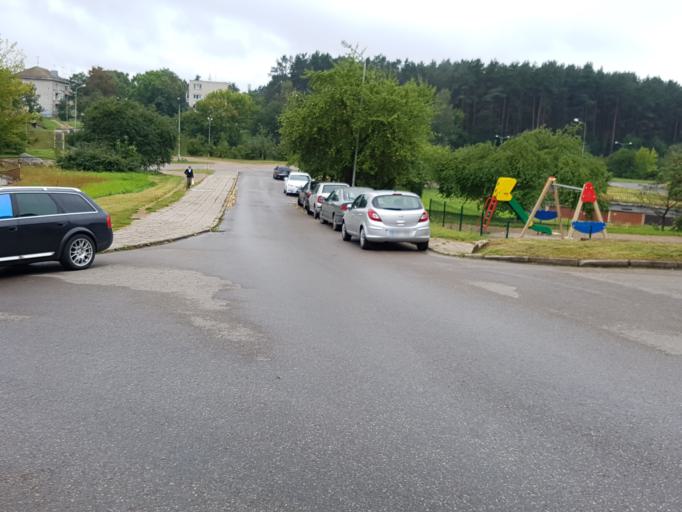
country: LT
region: Vilnius County
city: Lazdynai
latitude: 54.6724
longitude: 25.2145
